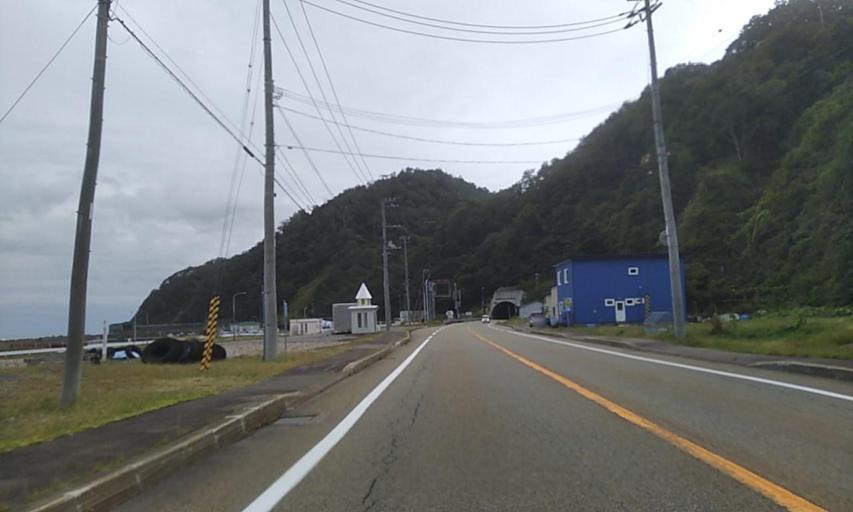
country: JP
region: Hokkaido
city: Obihiro
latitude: 42.1219
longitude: 143.3156
